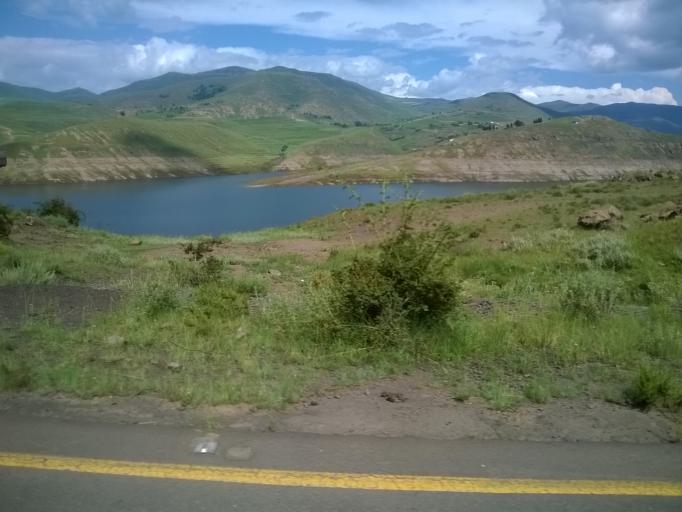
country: LS
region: Thaba-Tseka
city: Thaba-Tseka
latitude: -29.1724
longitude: 28.4809
